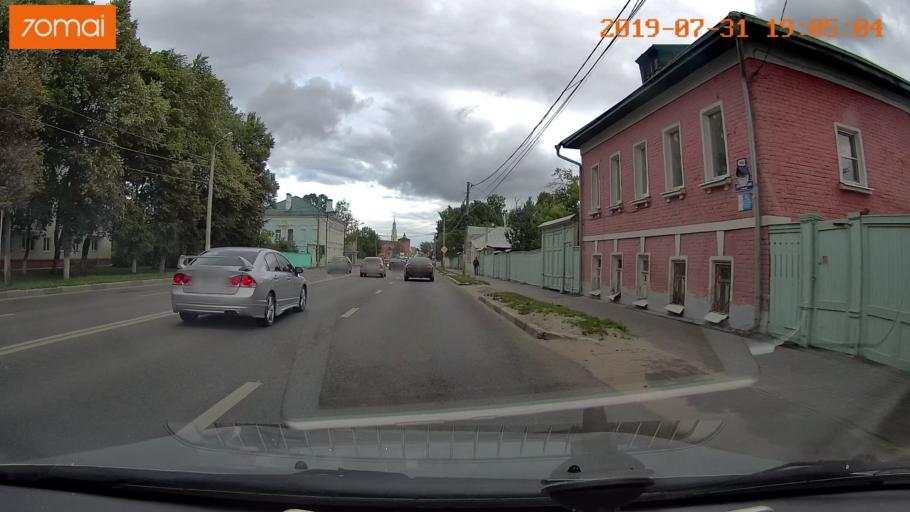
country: RU
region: Moskovskaya
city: Raduzhnyy
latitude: 55.1069
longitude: 38.7445
